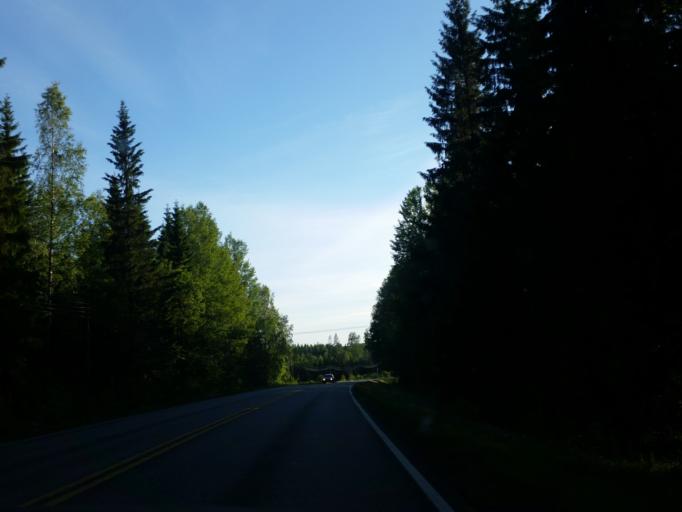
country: FI
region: Northern Savo
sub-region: Kuopio
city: Kuopio
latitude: 62.8456
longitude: 27.3731
